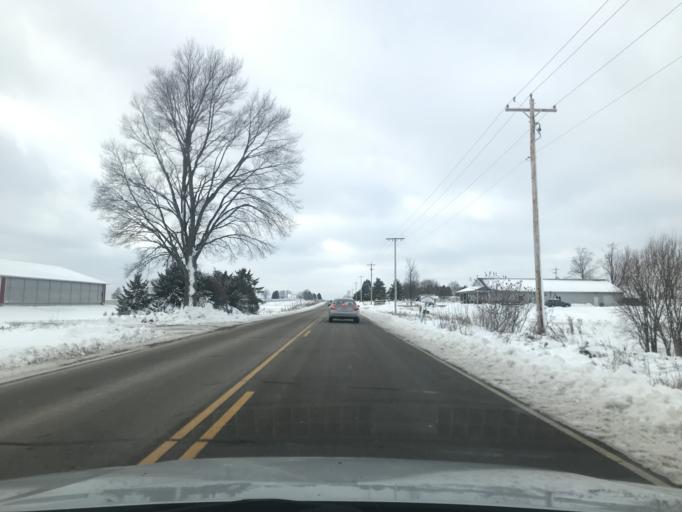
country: US
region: Wisconsin
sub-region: Oconto County
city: Oconto
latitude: 44.9498
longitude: -87.9169
